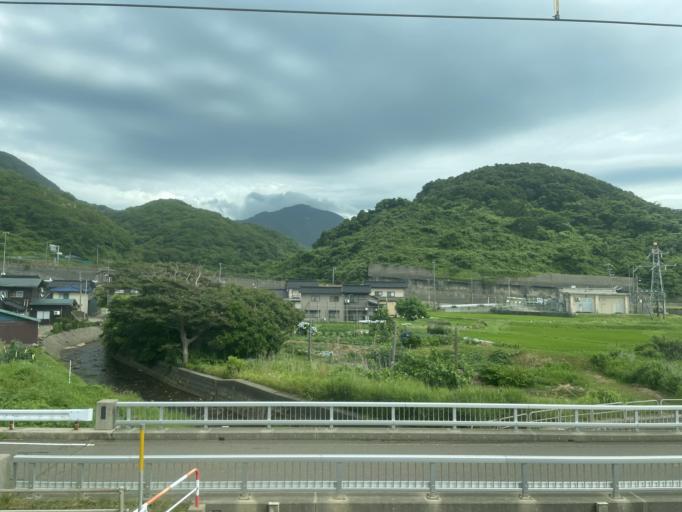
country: JP
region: Niigata
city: Kashiwazaki
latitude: 37.3190
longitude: 138.4341
